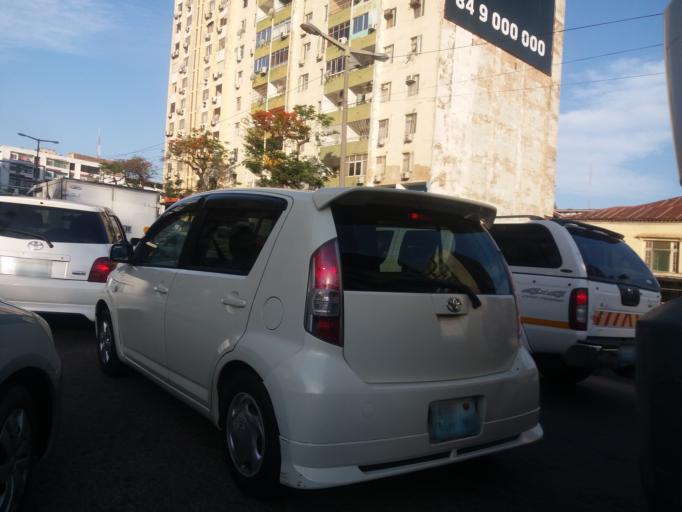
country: MZ
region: Maputo City
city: Maputo
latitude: -25.9620
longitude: 32.5694
